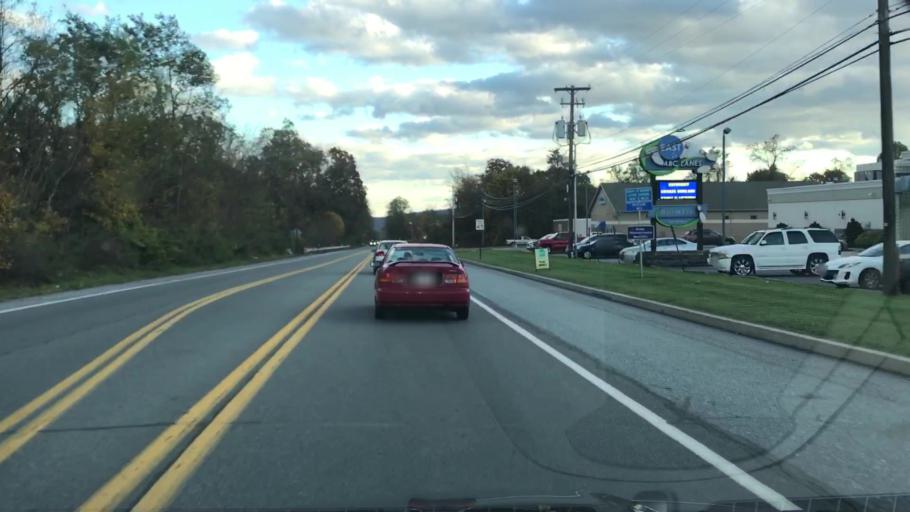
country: US
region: Pennsylvania
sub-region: Dauphin County
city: Bressler
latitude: 40.2381
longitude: -76.8044
